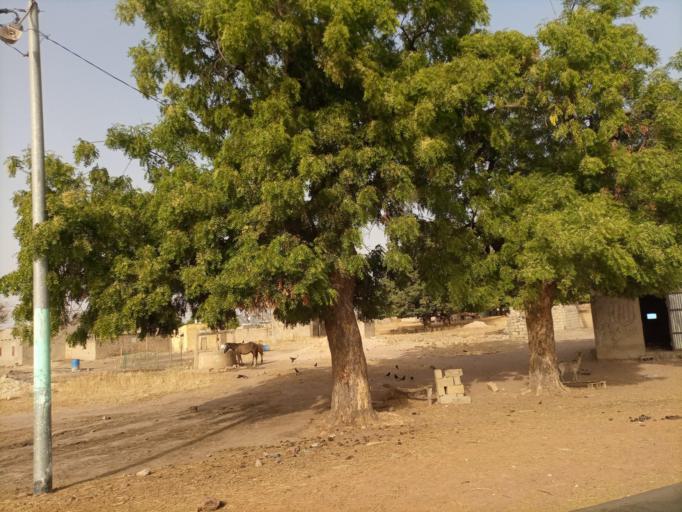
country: SN
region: Fatick
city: Passi
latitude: 14.0341
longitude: -16.3144
